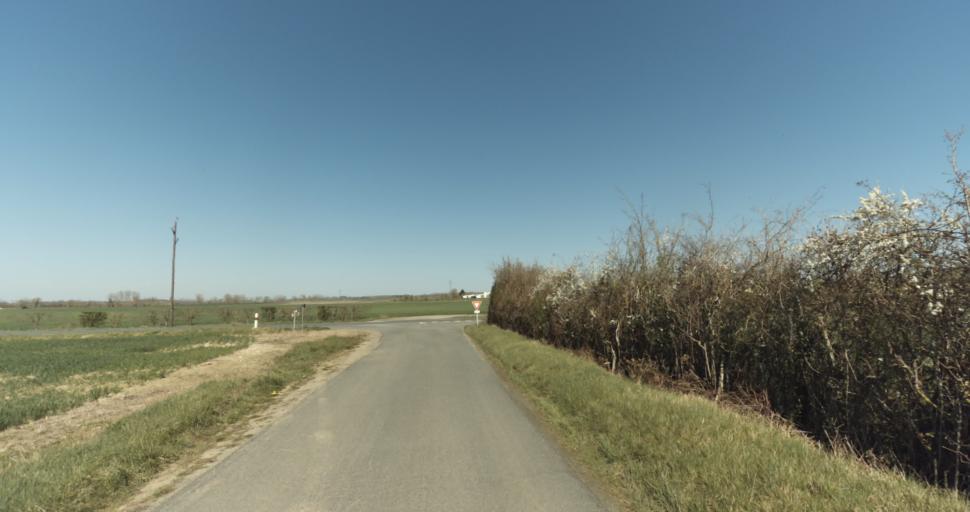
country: FR
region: Lower Normandy
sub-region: Departement du Calvados
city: Saint-Pierre-sur-Dives
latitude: 49.0179
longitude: 0.0294
